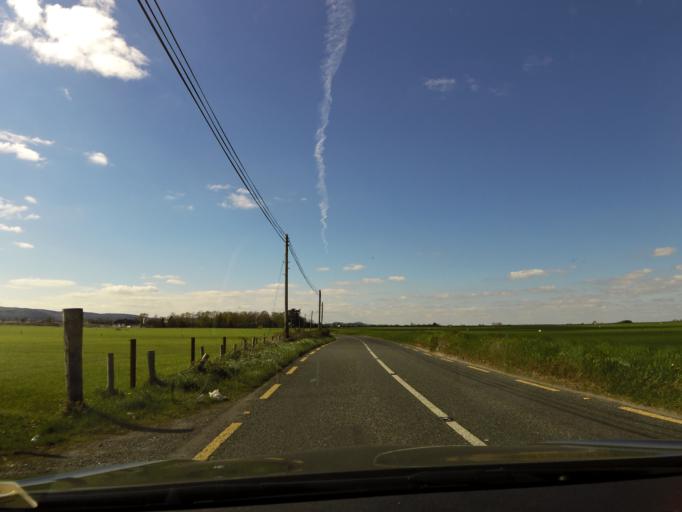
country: IE
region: Leinster
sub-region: Kildare
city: Athy
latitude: 53.0011
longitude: -7.0242
